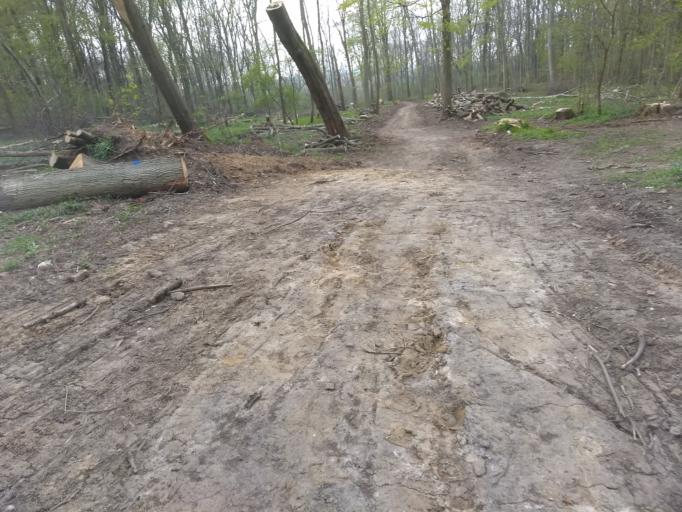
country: FR
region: Nord-Pas-de-Calais
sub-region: Departement du Pas-de-Calais
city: Mont-Saint-Eloi
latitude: 50.3375
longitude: 2.6970
